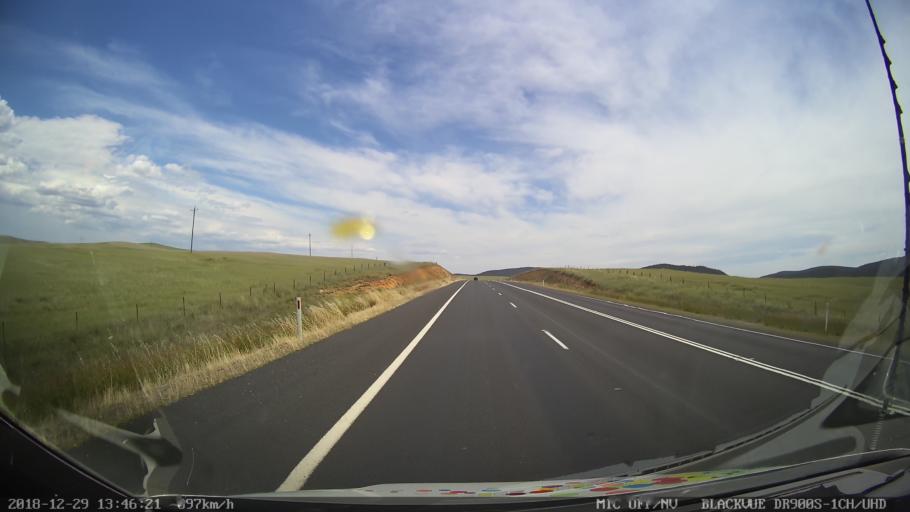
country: AU
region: New South Wales
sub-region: Cooma-Monaro
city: Cooma
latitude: -36.1103
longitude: 149.1429
